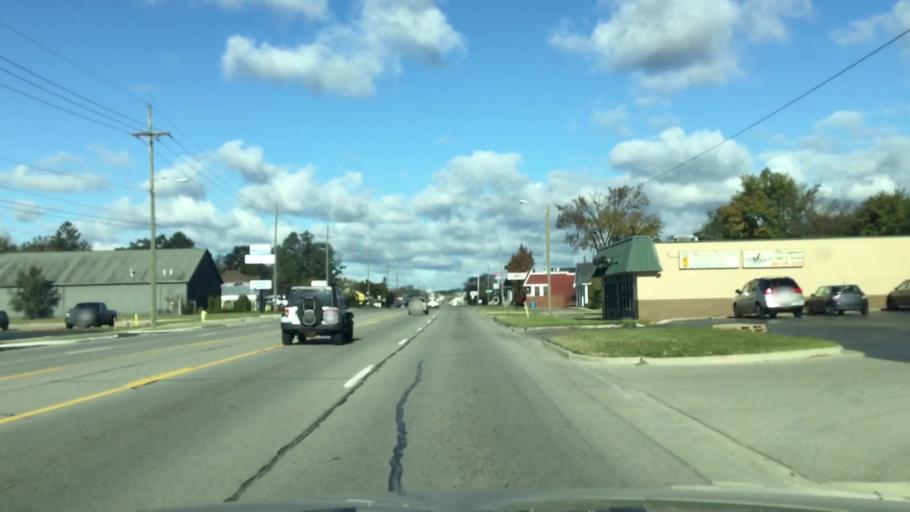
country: US
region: Michigan
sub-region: Oakland County
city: Waterford
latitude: 42.6851
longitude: -83.3788
